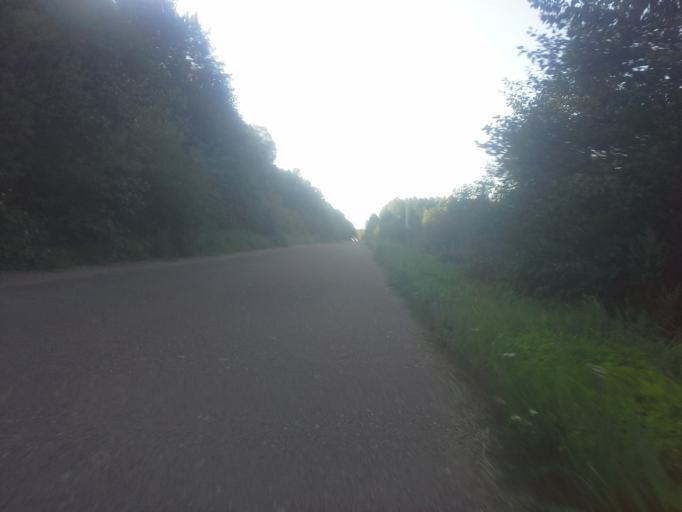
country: RU
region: Moskovskaya
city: Kievskij
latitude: 55.3820
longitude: 36.9092
